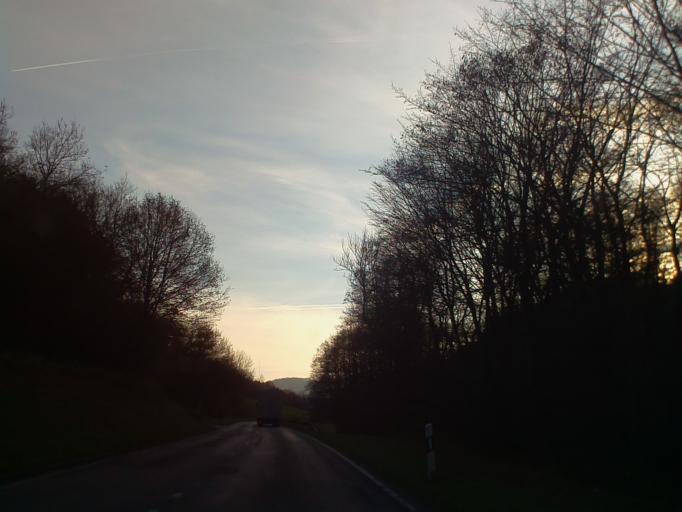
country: DE
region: Bavaria
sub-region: Regierungsbezirk Unterfranken
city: Kirchzell
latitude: 49.6321
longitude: 9.2109
